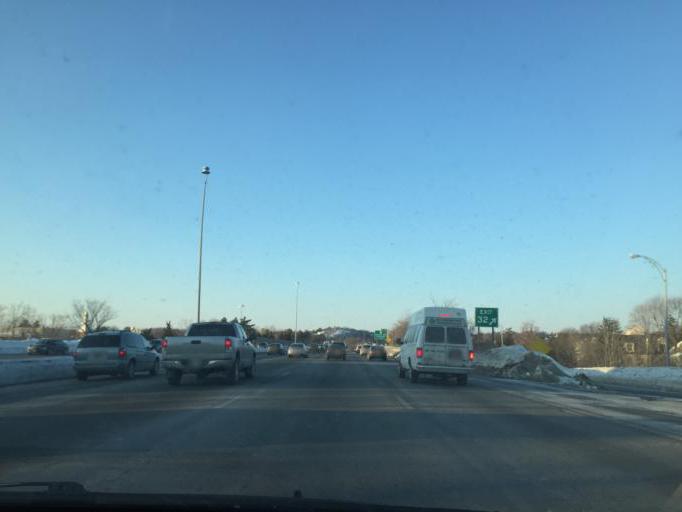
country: US
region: Massachusetts
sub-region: Middlesex County
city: Medford
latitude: 42.4171
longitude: -71.1039
